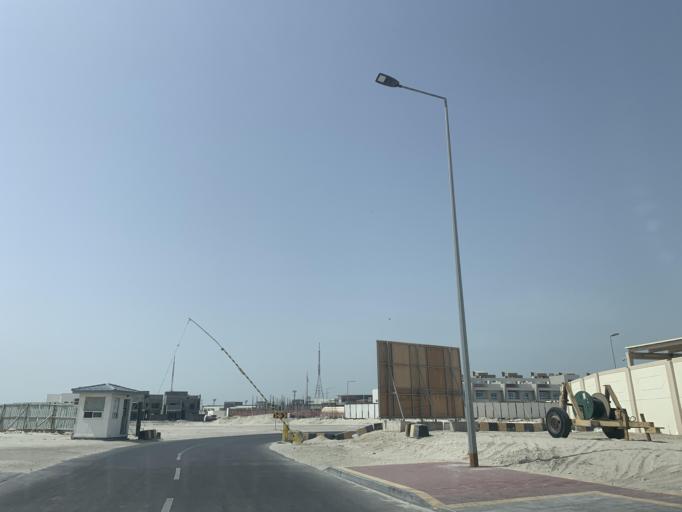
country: BH
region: Northern
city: Ar Rifa'
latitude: 26.1530
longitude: 50.5629
